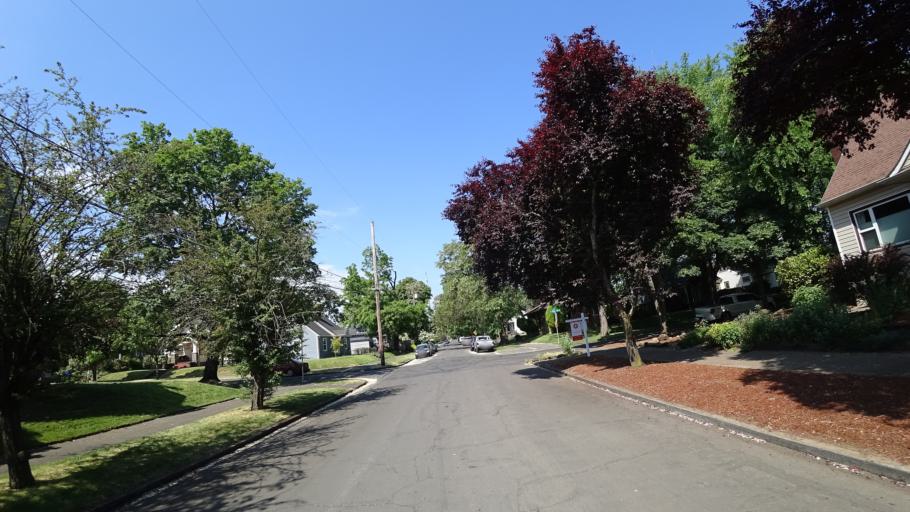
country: US
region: Oregon
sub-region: Multnomah County
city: Portland
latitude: 45.5677
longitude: -122.6655
